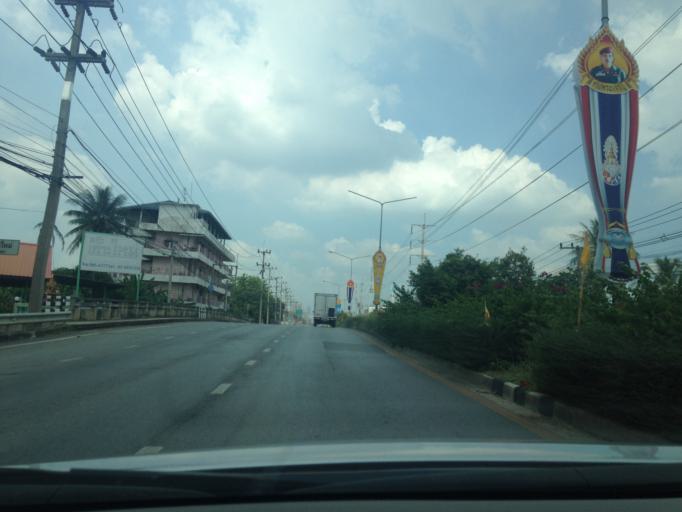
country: TH
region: Pathum Thani
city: Sam Khok
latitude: 14.0582
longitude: 100.5240
